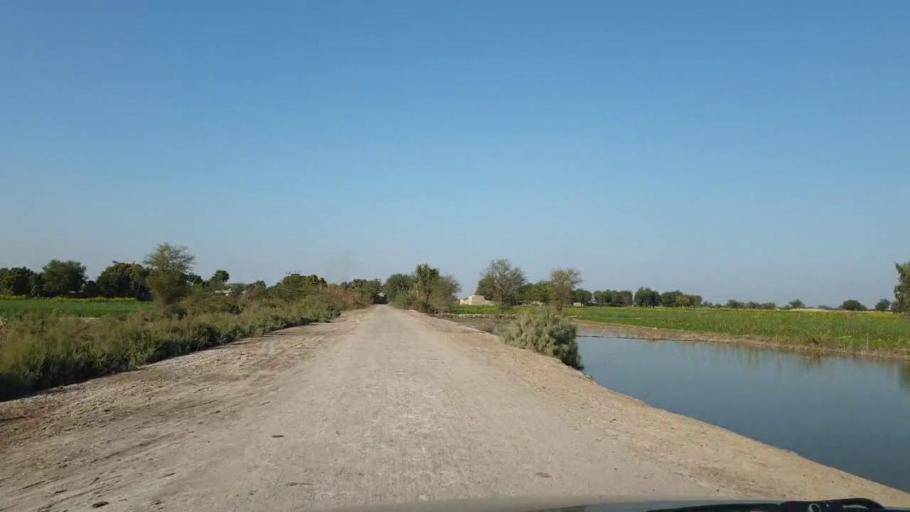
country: PK
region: Sindh
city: Khadro
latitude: 26.2125
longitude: 68.7542
